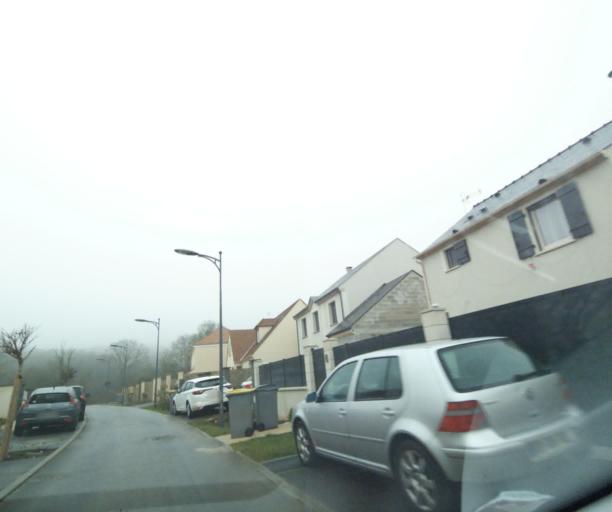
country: FR
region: Ile-de-France
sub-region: Departement de Seine-et-Marne
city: Dammartin-en-Goele
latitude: 49.0617
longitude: 2.6733
